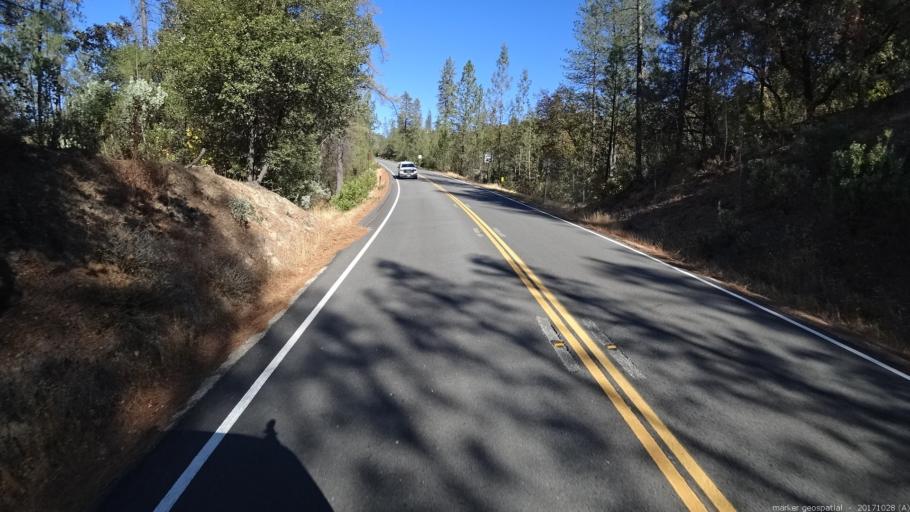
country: US
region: California
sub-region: Shasta County
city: Shasta
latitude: 40.6083
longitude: -122.5278
